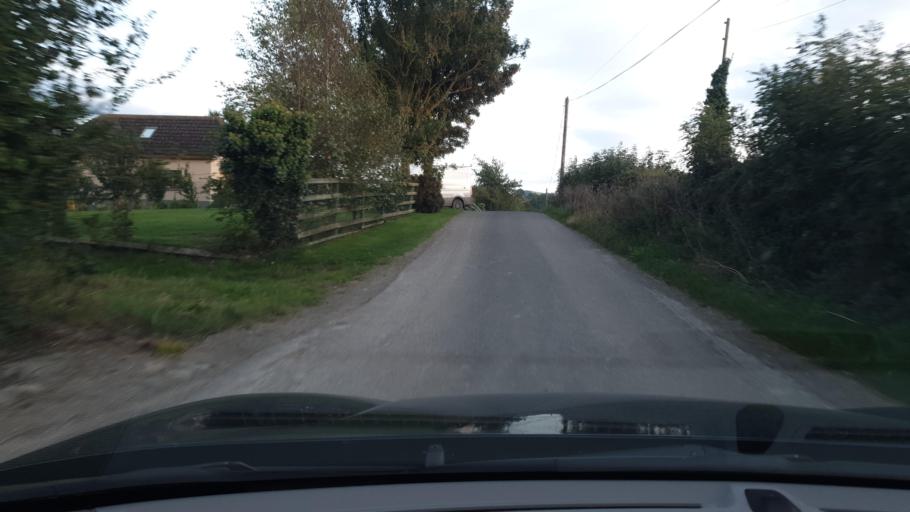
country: IE
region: Leinster
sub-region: An Mhi
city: Stamullin
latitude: 53.5811
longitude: -6.2452
